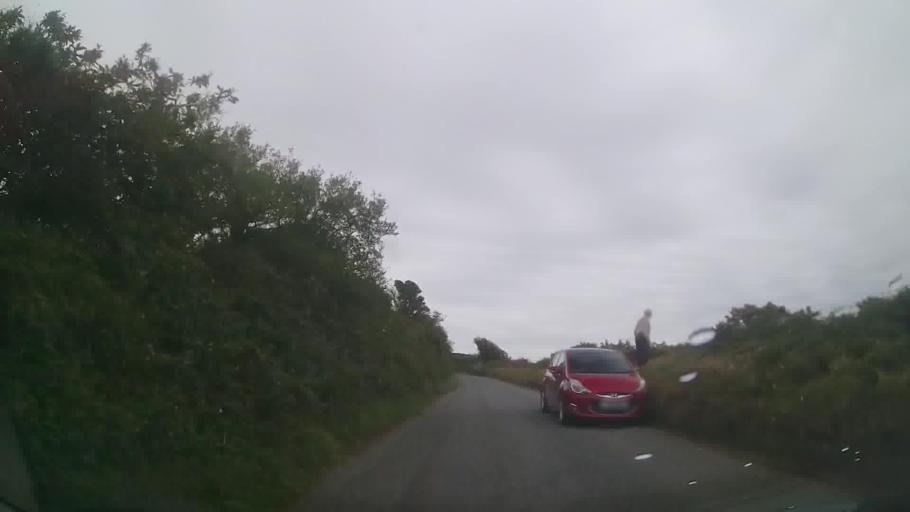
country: GB
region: Wales
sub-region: Pembrokeshire
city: Saundersfoot
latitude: 51.7349
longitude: -4.6409
